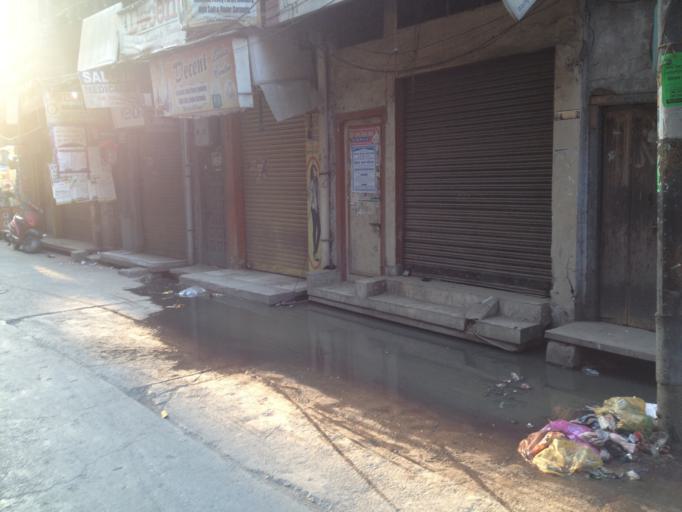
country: IN
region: Punjab
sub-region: Amritsar
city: Amritsar
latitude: 31.6183
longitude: 74.8743
